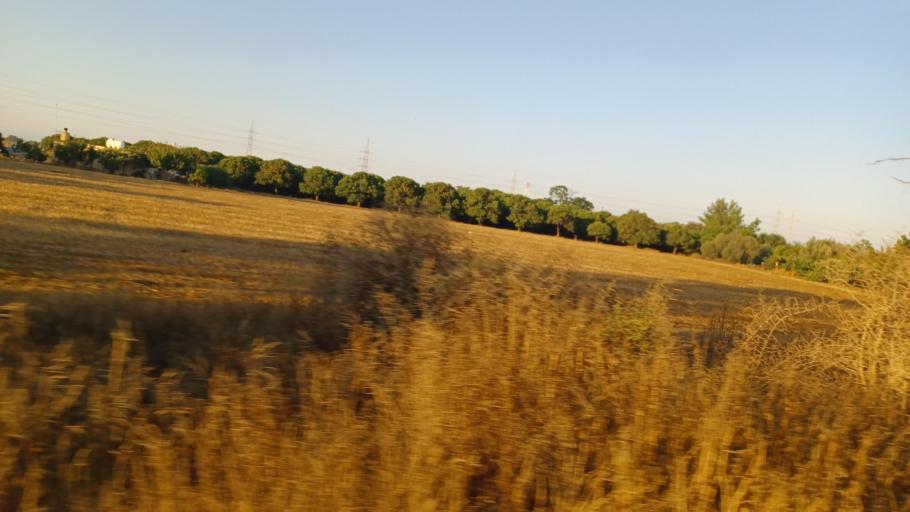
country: CY
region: Larnaka
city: Xylotymbou
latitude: 35.0048
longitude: 33.7866
